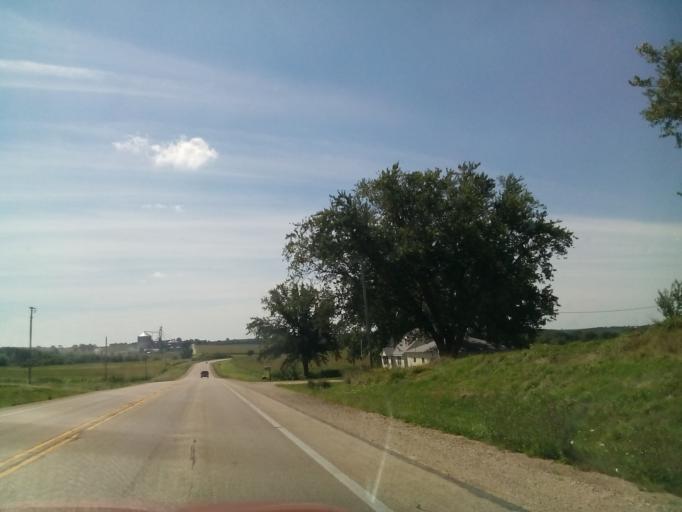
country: US
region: Wisconsin
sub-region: Green County
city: Monticello
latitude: 42.7206
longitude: -89.5983
